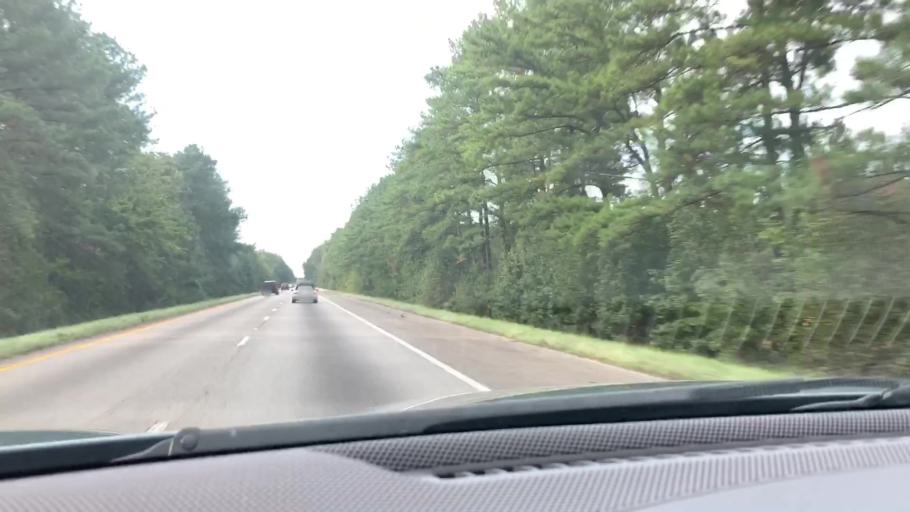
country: US
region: South Carolina
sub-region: Dorchester County
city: Saint George
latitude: 33.3397
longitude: -80.5700
